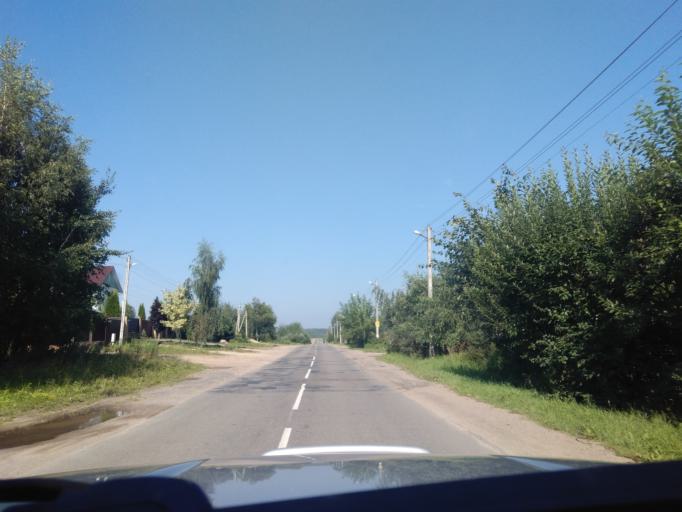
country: BY
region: Minsk
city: Zhdanovichy
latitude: 53.9327
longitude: 27.4126
